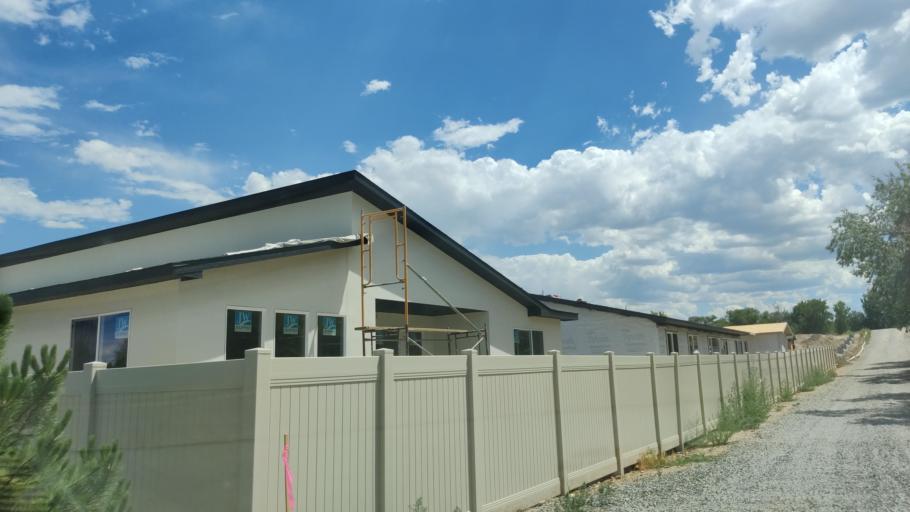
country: US
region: Colorado
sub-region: Mesa County
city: Orchard Mesa
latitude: 39.0374
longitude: -108.5467
